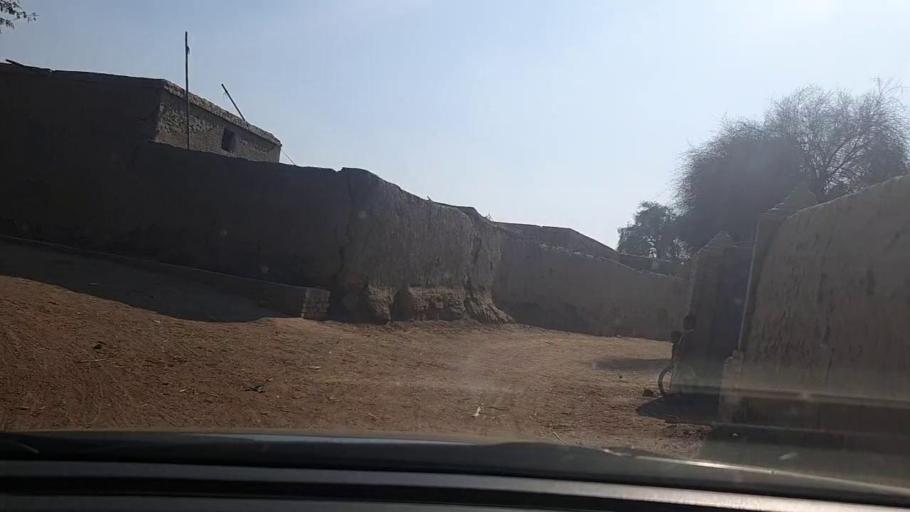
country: PK
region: Sindh
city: Sann
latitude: 26.2689
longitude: 68.0715
